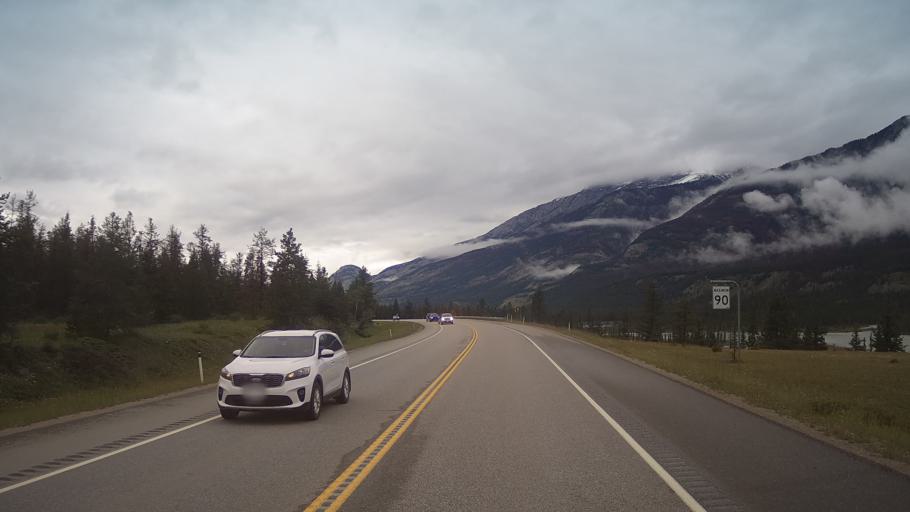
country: CA
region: Alberta
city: Jasper Park Lodge
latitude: 52.9460
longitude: -118.0396
